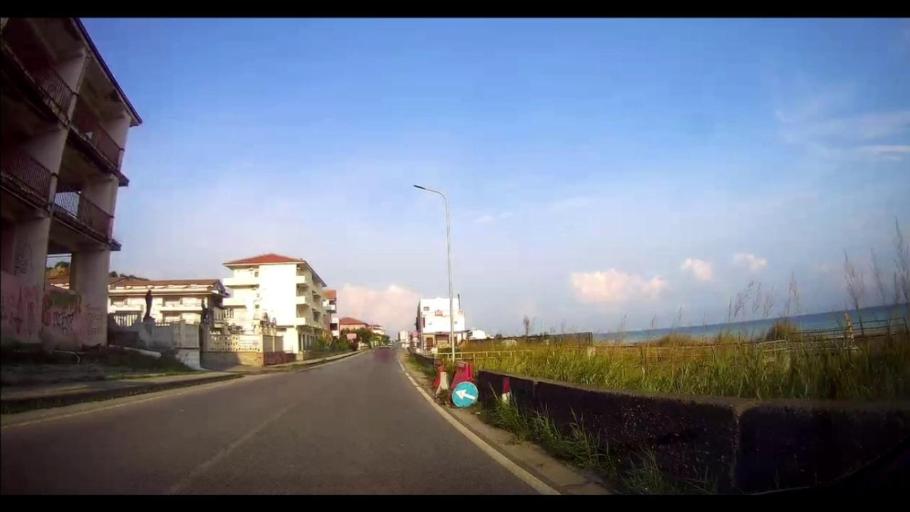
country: IT
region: Calabria
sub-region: Provincia di Cosenza
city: Cariati
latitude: 39.5089
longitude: 16.9319
